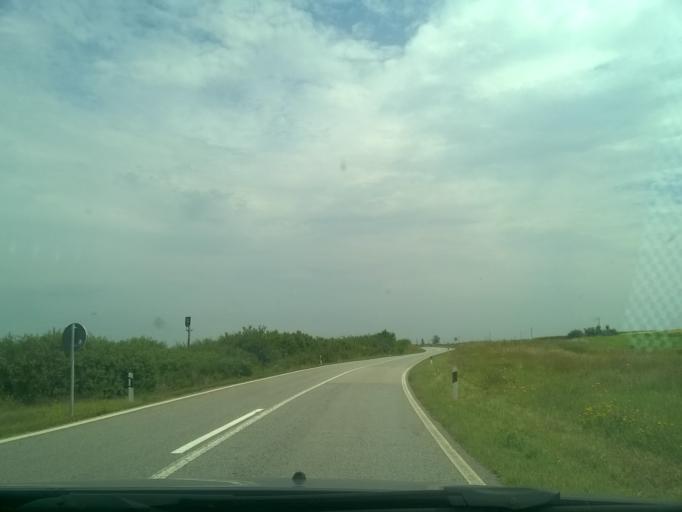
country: RS
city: Boka
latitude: 45.3480
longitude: 20.8107
